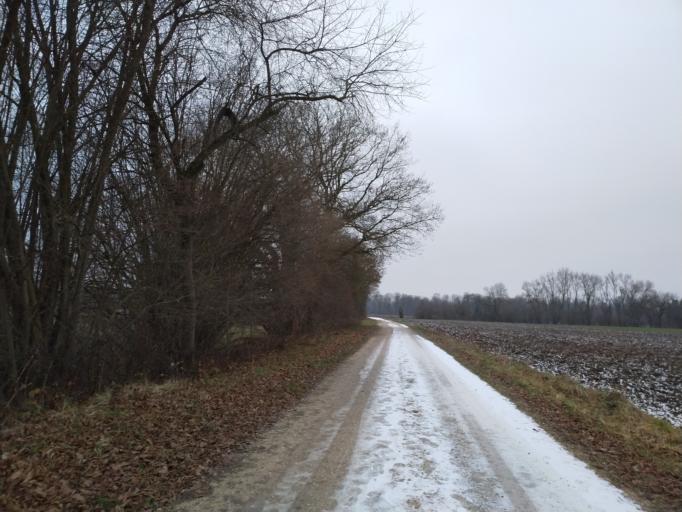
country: DE
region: Bavaria
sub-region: Swabia
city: Offingen
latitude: 48.4934
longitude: 10.3503
